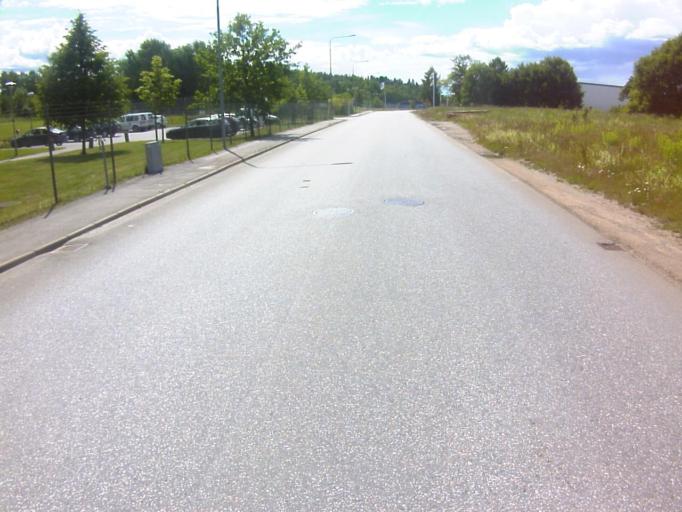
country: SE
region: Soedermanland
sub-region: Eskilstuna Kommun
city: Skogstorp
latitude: 59.3485
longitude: 16.4750
